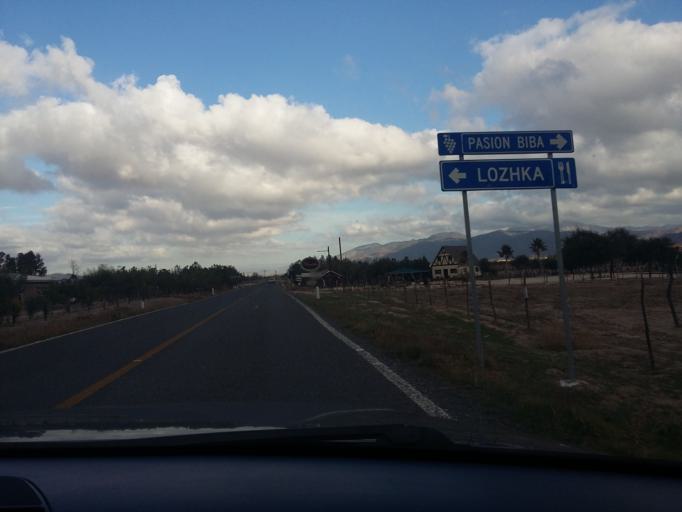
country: MX
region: Baja California
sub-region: Ensenada
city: Rancho Verde
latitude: 32.0491
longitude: -116.6621
